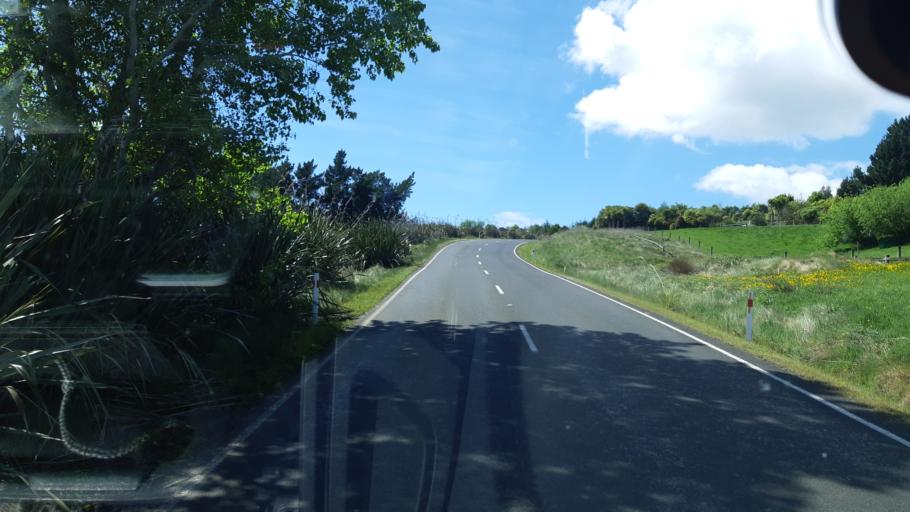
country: NZ
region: Otago
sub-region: Dunedin City
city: Portobello
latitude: -45.7706
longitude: 170.5803
